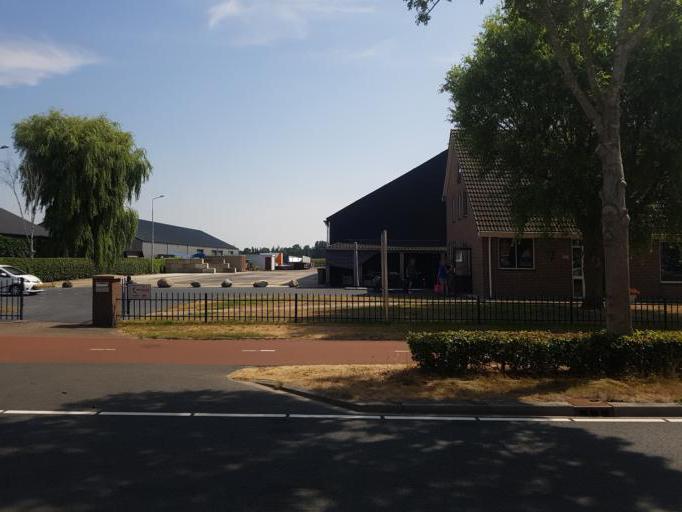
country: NL
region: Overijssel
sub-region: Gemeente Steenwijkerland
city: Giethoorn
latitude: 52.7234
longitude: 6.0775
